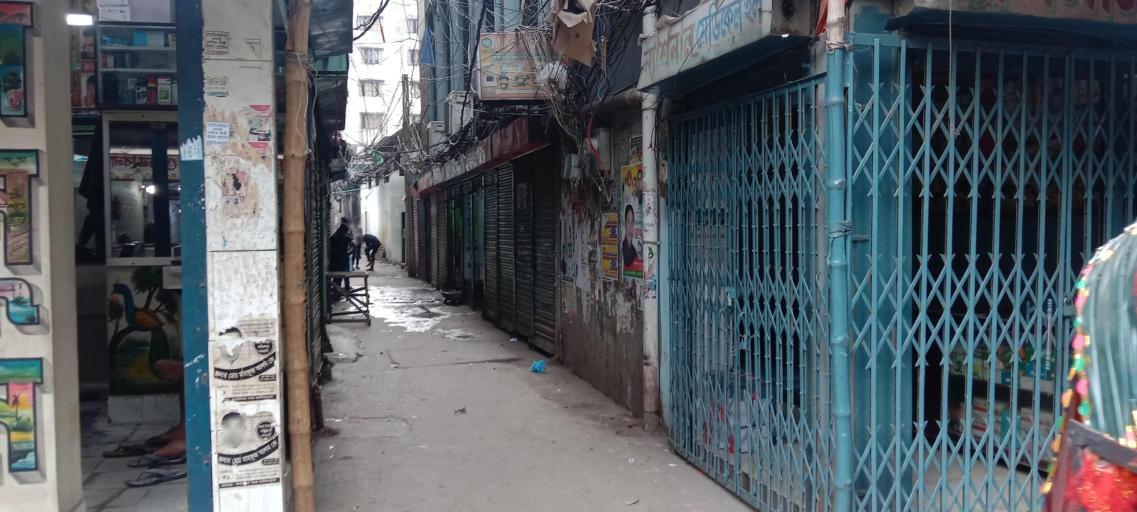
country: BD
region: Dhaka
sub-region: Dhaka
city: Dhaka
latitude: 23.7020
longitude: 90.4091
